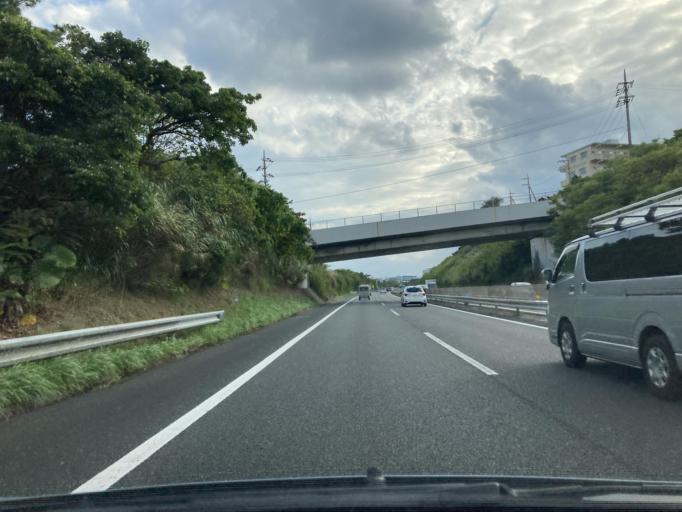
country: JP
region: Okinawa
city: Ginowan
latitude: 26.2655
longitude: 127.7740
